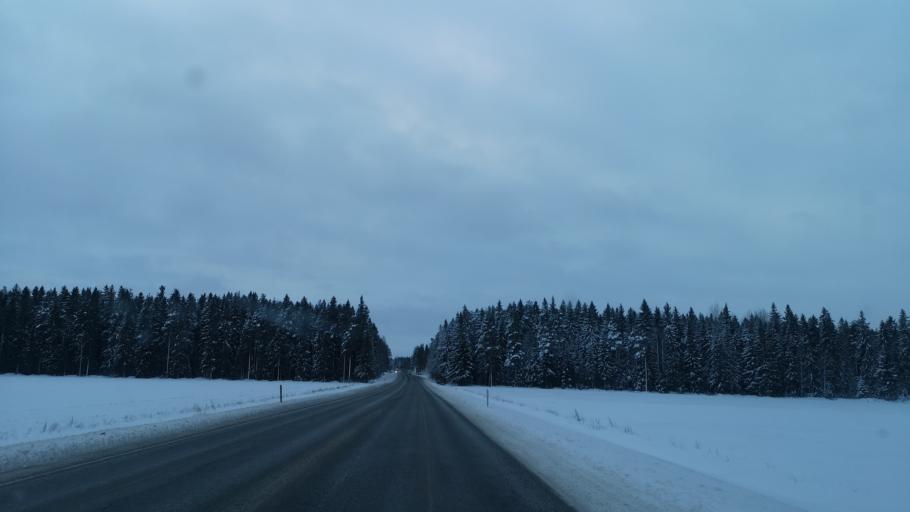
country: FI
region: Varsinais-Suomi
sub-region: Loimaa
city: Loimaa
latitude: 60.8795
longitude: 23.0768
